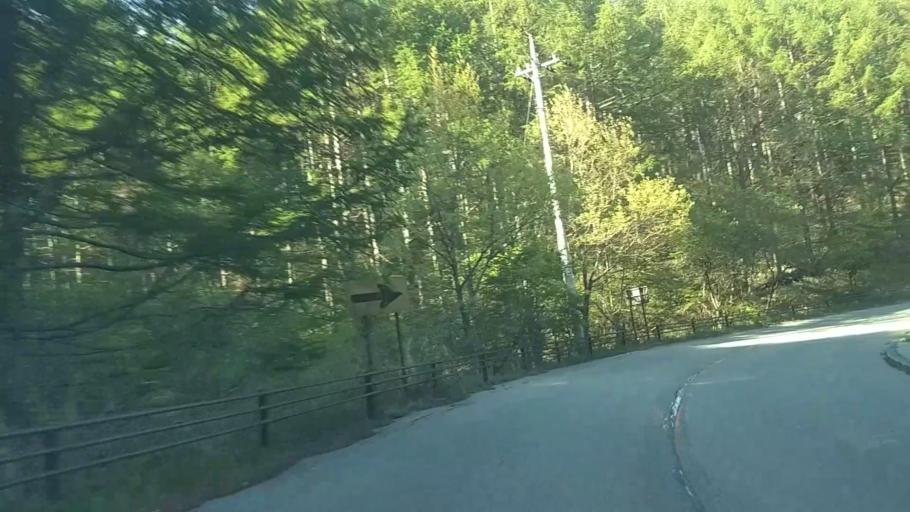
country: JP
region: Yamanashi
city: Nirasaki
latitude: 35.9130
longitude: 138.4010
